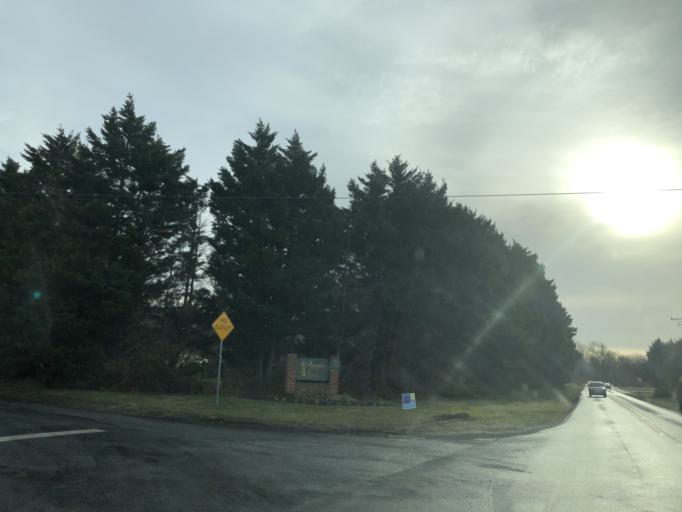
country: US
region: Delaware
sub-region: New Castle County
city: Middletown
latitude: 39.4500
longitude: -75.6503
